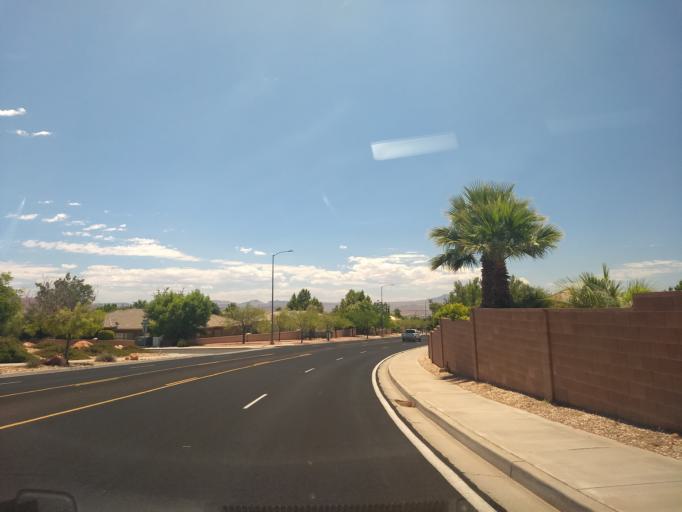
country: US
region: Utah
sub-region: Washington County
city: Washington
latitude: 37.1437
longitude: -113.5289
